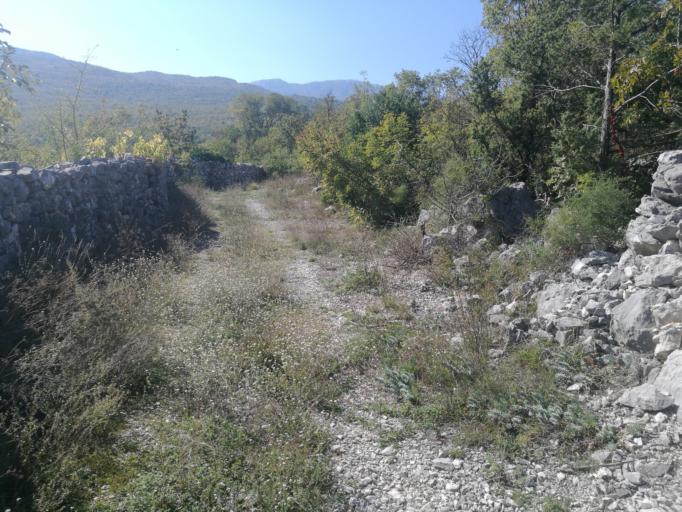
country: HR
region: Splitsko-Dalmatinska
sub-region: Grad Omis
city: Omis
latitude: 43.5173
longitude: 16.7320
